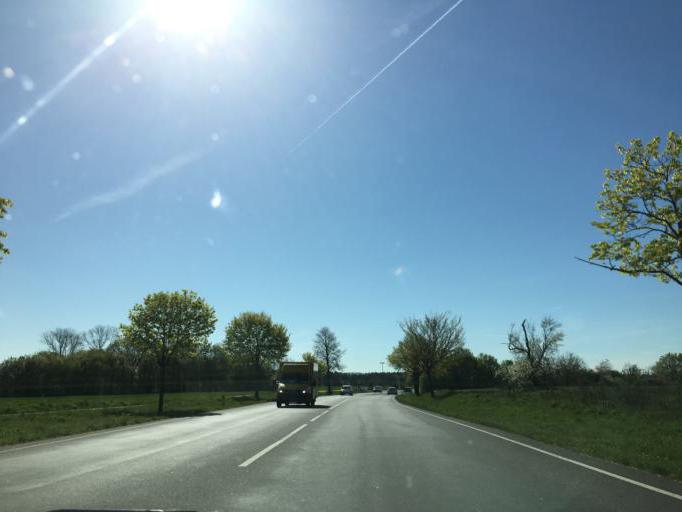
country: DE
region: Hesse
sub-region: Regierungsbezirk Darmstadt
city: Rodgau
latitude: 50.0131
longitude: 8.8723
